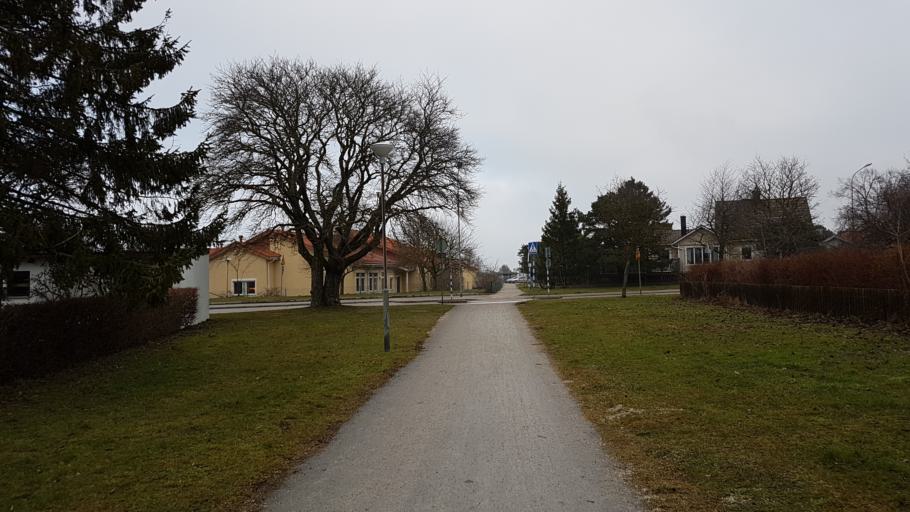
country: SE
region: Gotland
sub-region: Gotland
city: Visby
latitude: 57.6360
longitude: 18.3188
